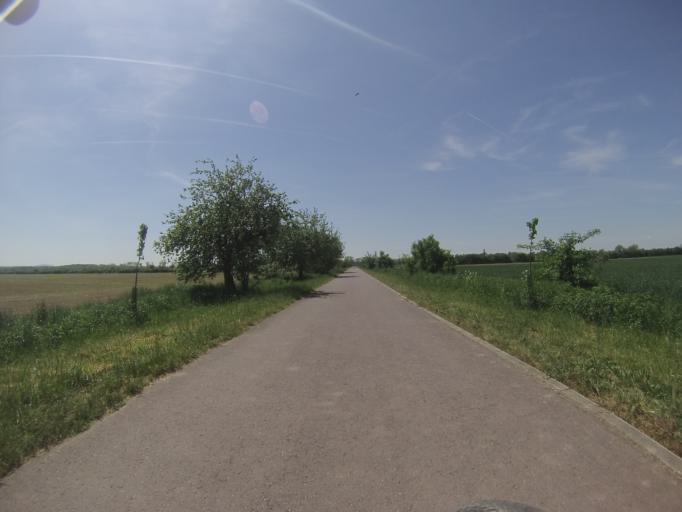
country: CZ
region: South Moravian
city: Zidlochovice
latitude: 49.0228
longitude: 16.6219
